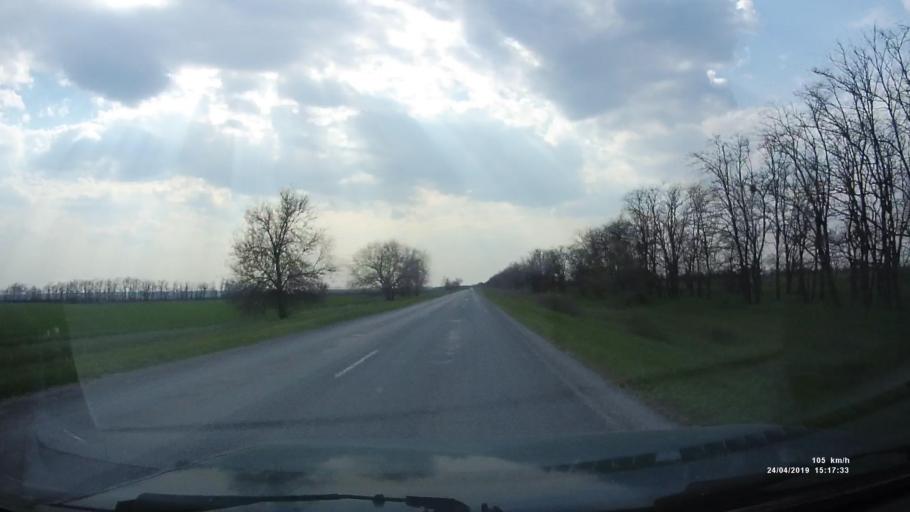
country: RU
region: Rostov
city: Remontnoye
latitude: 46.5465
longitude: 43.1870
